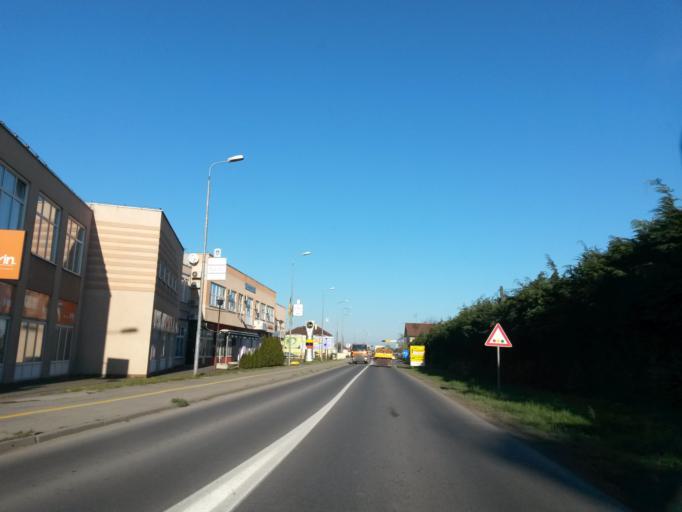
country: HR
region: Koprivnicko-Krizevacka
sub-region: Grad Koprivnica
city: Koprivnica
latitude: 46.1671
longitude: 16.8167
